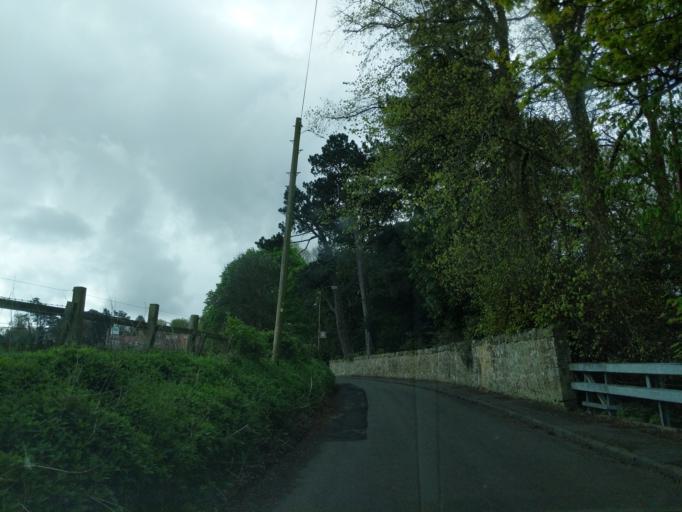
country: GB
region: Scotland
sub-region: Edinburgh
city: Currie
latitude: 55.8957
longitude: -3.3009
